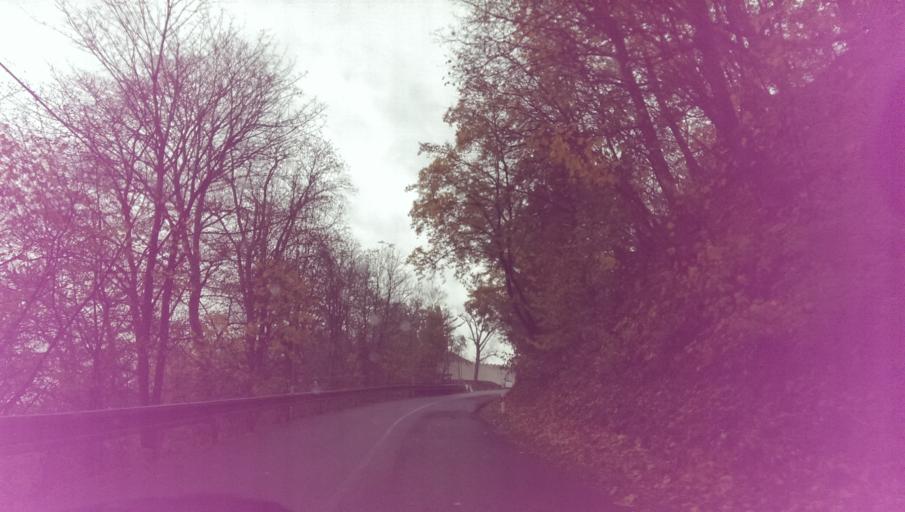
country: AT
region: Lower Austria
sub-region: Politischer Bezirk Hollabrunn
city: Hardegg
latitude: 48.8937
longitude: 15.8080
